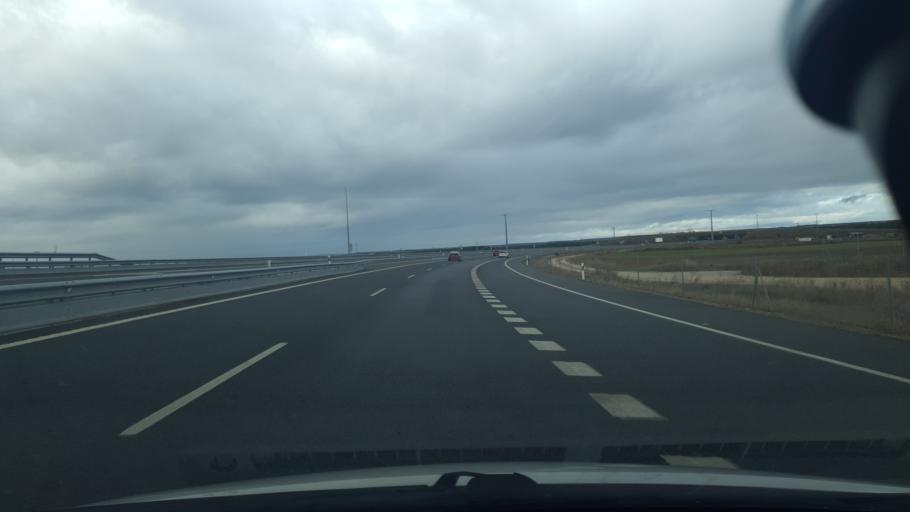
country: ES
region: Castille and Leon
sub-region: Provincia de Segovia
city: Sanchonuno
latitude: 41.3175
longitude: -4.3105
